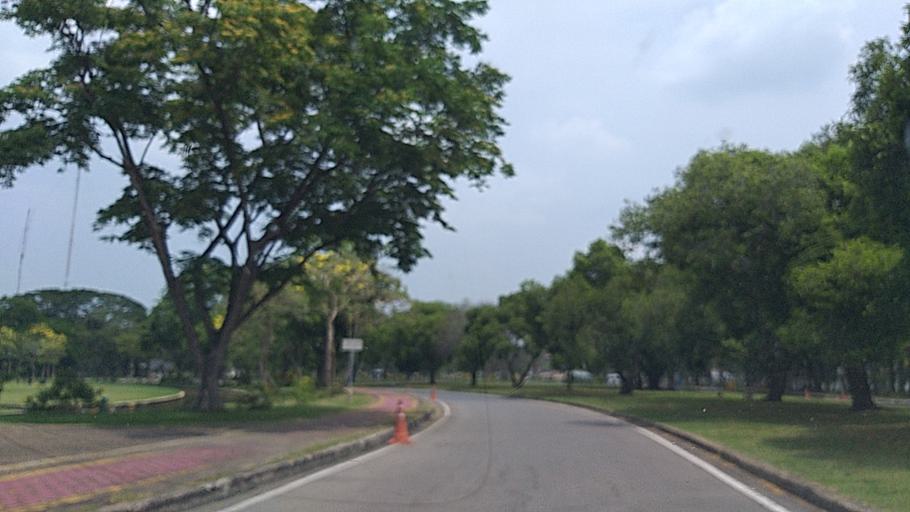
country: TH
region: Bangkok
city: Thawi Watthana
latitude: 13.7806
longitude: 100.3253
